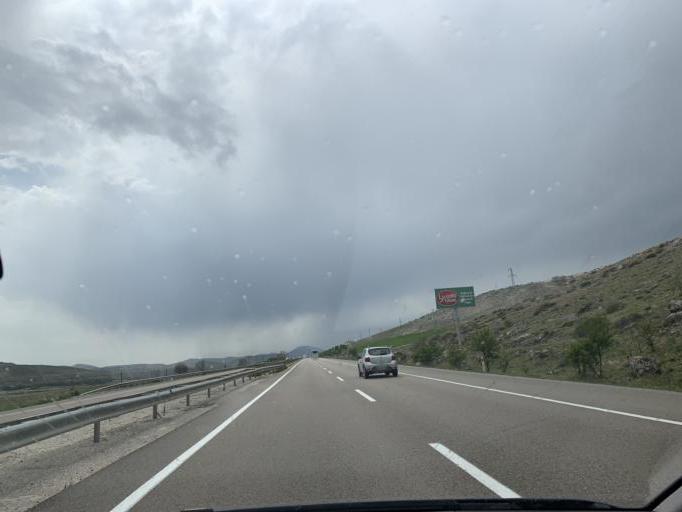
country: TR
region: Eskisehir
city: Sivrihisar
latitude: 39.5415
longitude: 31.7020
